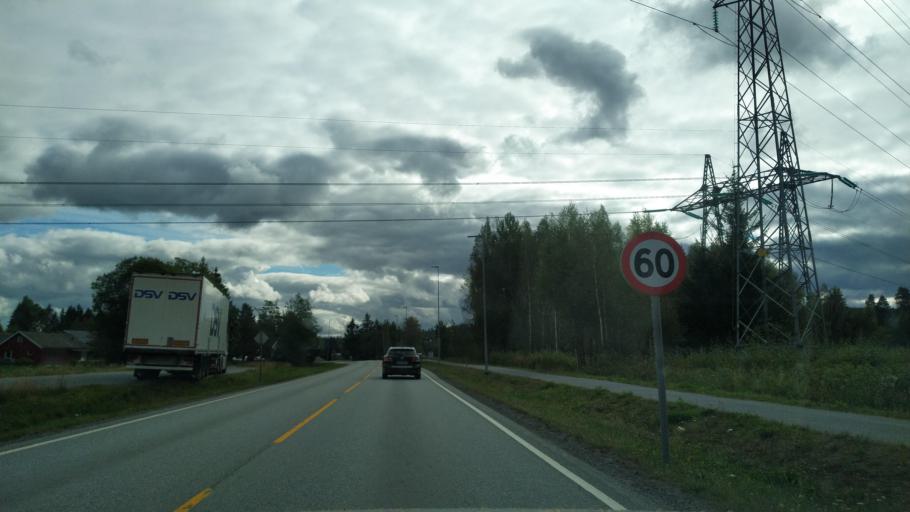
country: NO
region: Akershus
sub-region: Sorum
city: Frogner
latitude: 60.0175
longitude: 11.1394
